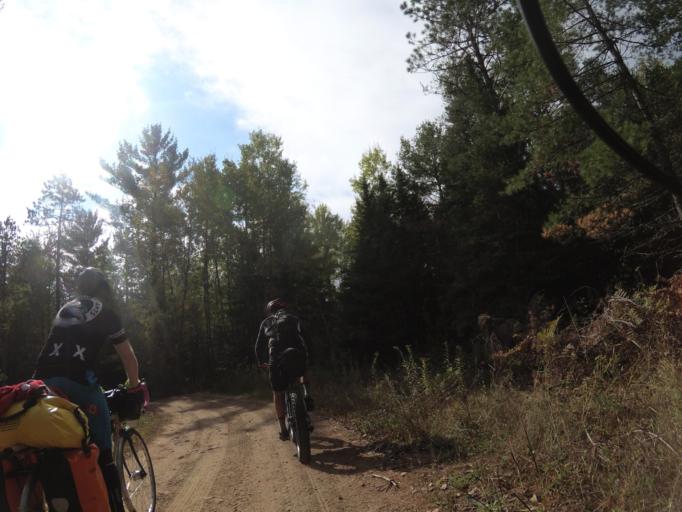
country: CA
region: Ontario
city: Pembroke
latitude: 45.2679
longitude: -77.2125
